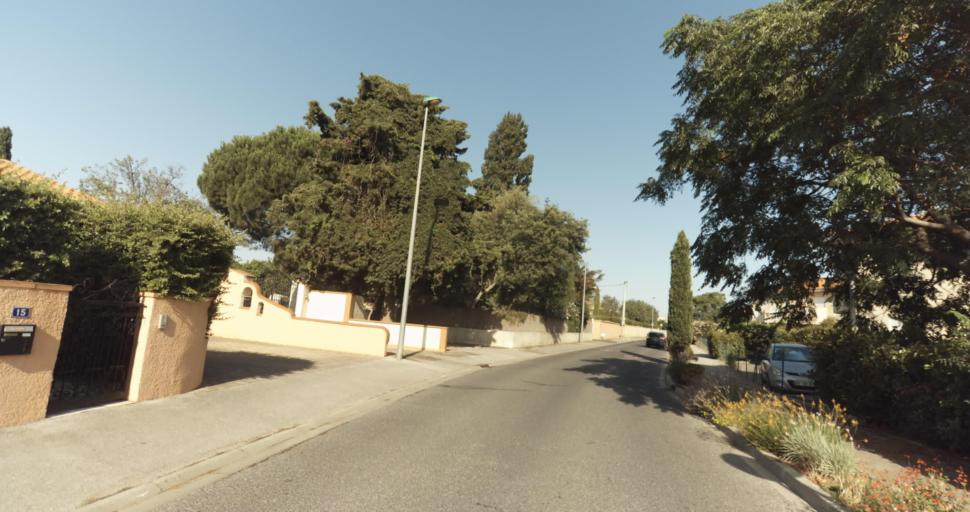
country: FR
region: Languedoc-Roussillon
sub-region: Departement des Pyrenees-Orientales
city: Alenya
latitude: 42.6422
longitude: 2.9786
